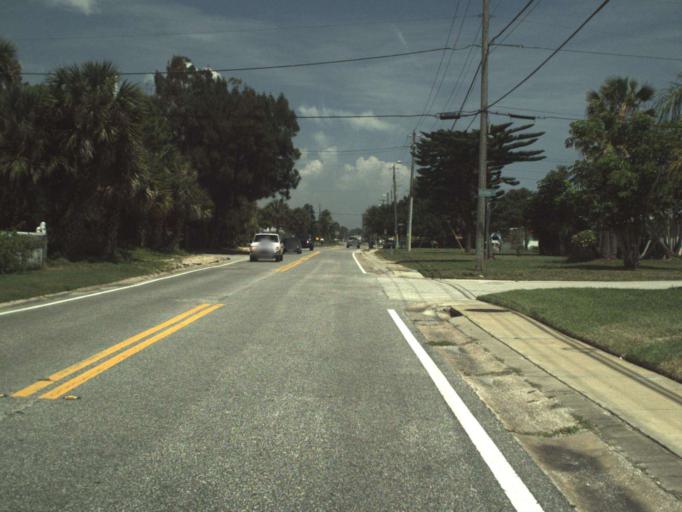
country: US
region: Florida
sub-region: Volusia County
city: Daytona Beach Shores
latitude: 29.1546
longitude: -80.9739
